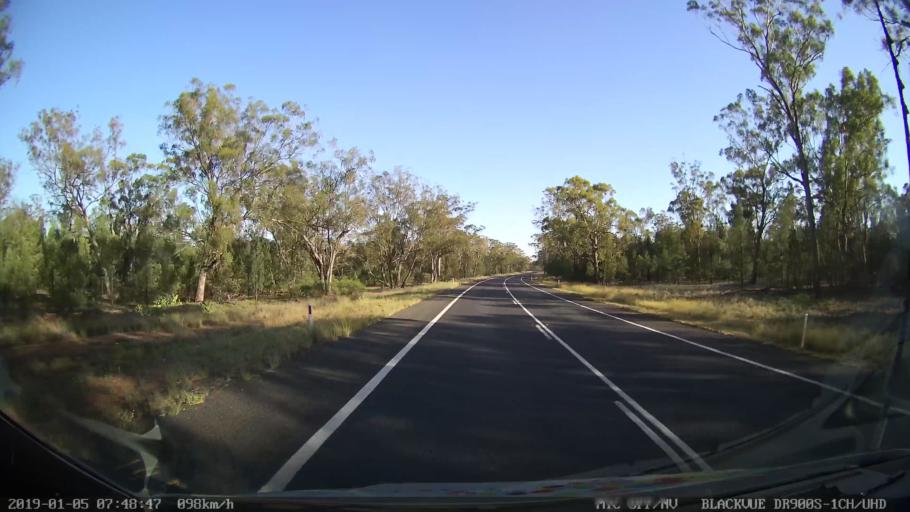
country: AU
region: New South Wales
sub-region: Gilgandra
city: Gilgandra
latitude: -31.8115
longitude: 148.6364
